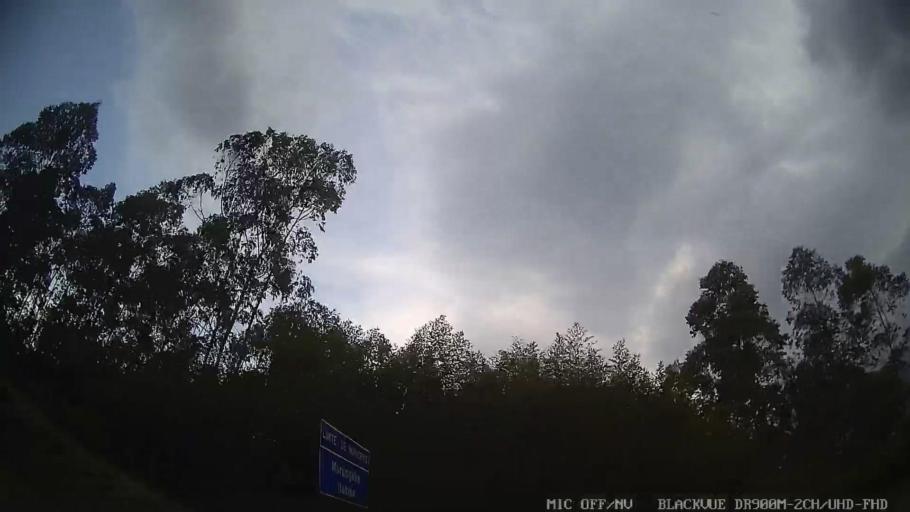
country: BR
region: Sao Paulo
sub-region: Itatiba
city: Itatiba
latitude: -22.9232
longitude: -46.7884
